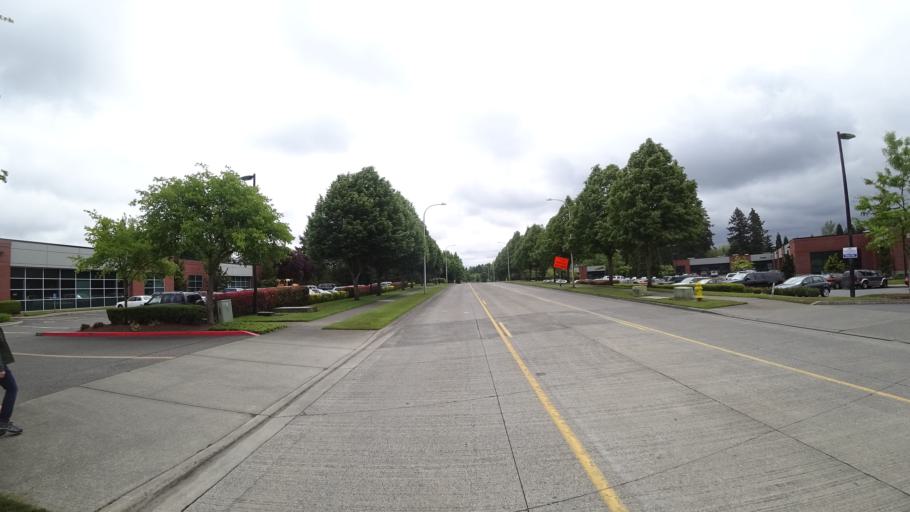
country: US
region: Oregon
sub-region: Washington County
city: Rockcreek
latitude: 45.5358
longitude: -122.8873
